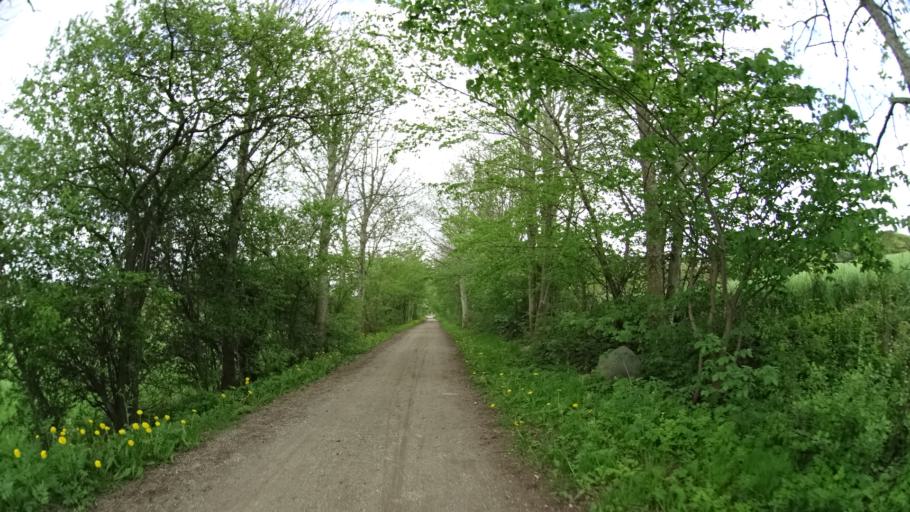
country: DK
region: Central Jutland
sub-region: Arhus Kommune
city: Stavtrup
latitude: 56.1398
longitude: 10.0883
